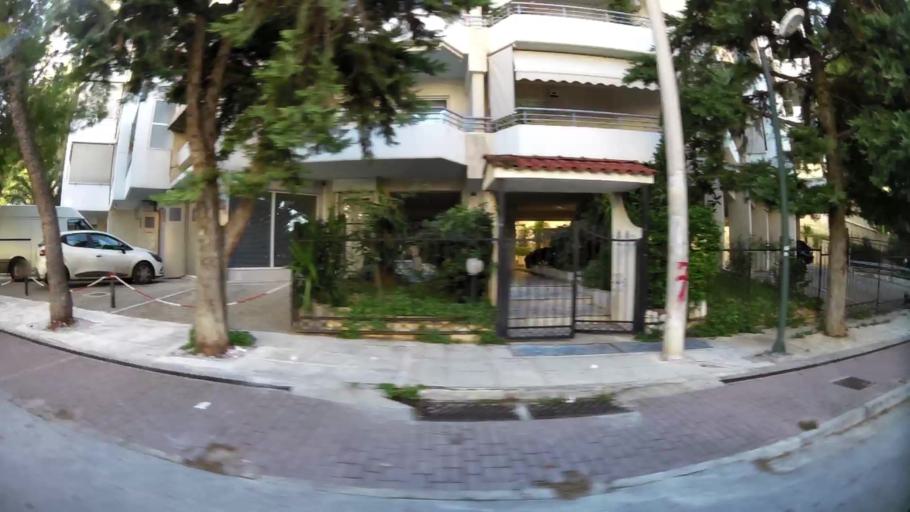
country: GR
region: Attica
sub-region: Nomarchia Athinas
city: Nea Erythraia
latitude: 38.0935
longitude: 23.8151
